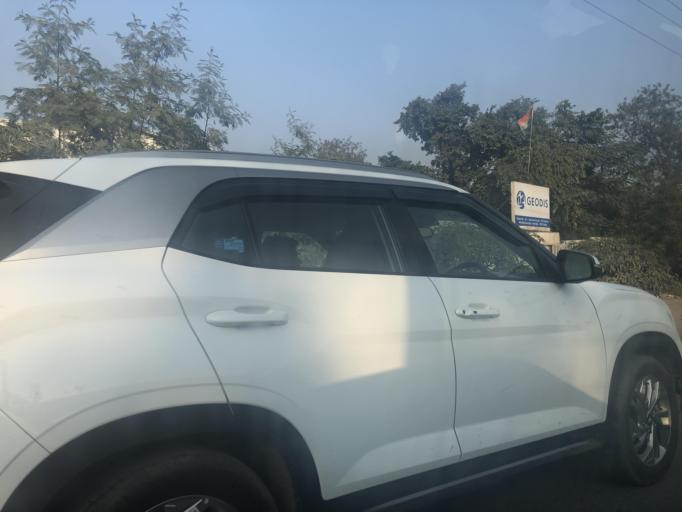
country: IN
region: Haryana
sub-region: Gurgaon
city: Gurgaon
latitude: 28.5391
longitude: 77.0308
